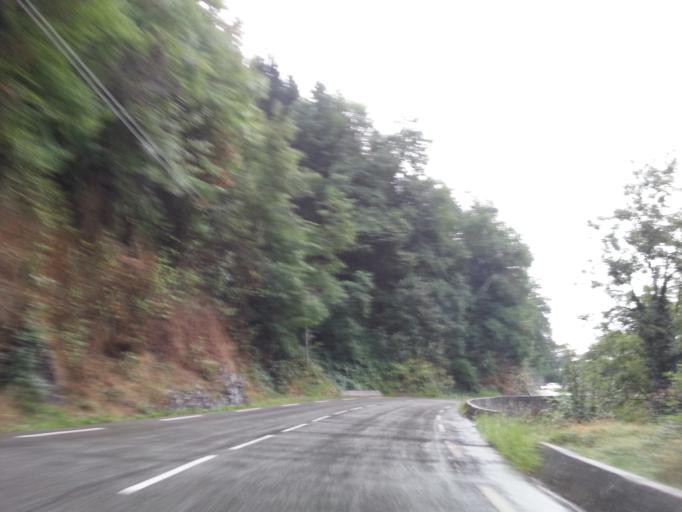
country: FR
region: Rhone-Alpes
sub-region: Departement de la Savoie
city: Marthod
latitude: 45.6966
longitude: 6.4266
